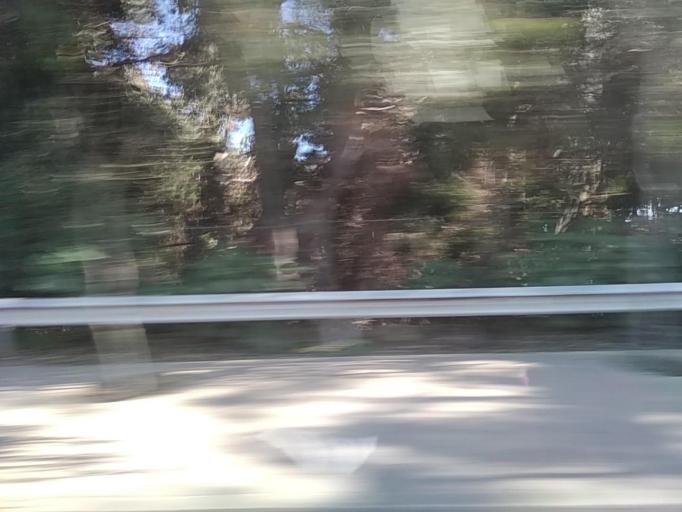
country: CL
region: Valparaiso
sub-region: San Antonio Province
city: El Tabo
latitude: -33.4389
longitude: -71.6841
